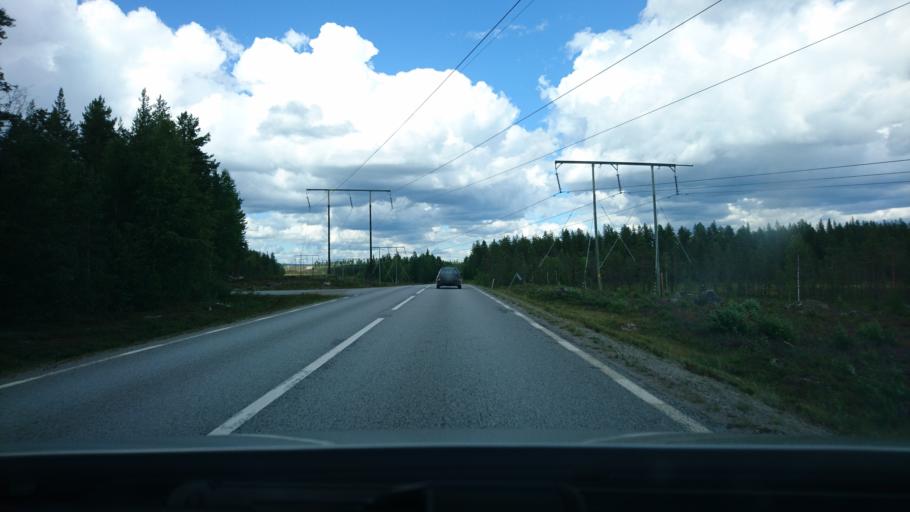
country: SE
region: Vaesterbotten
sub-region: Asele Kommun
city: Asele
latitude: 63.7357
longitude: 16.9918
